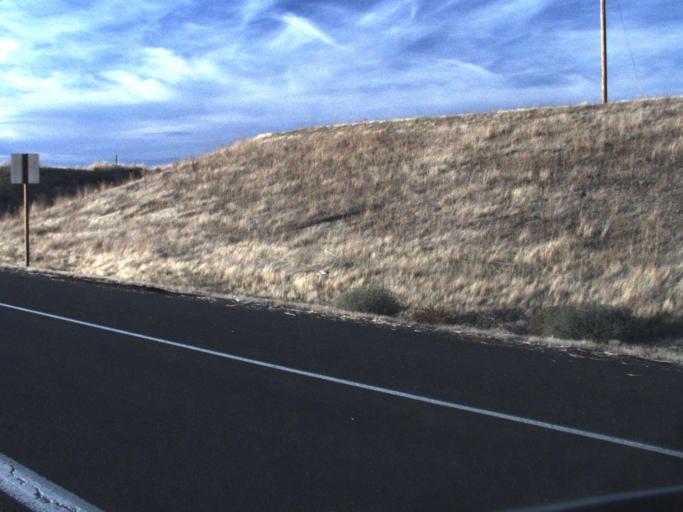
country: US
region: Washington
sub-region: Walla Walla County
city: Garrett
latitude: 46.0492
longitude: -118.4904
